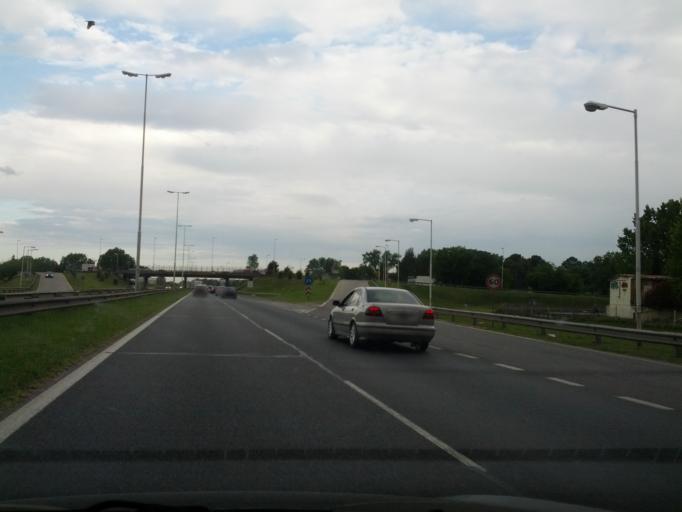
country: AR
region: Buenos Aires
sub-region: Partido de General Rodriguez
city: General Rodriguez
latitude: -34.5955
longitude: -58.9389
